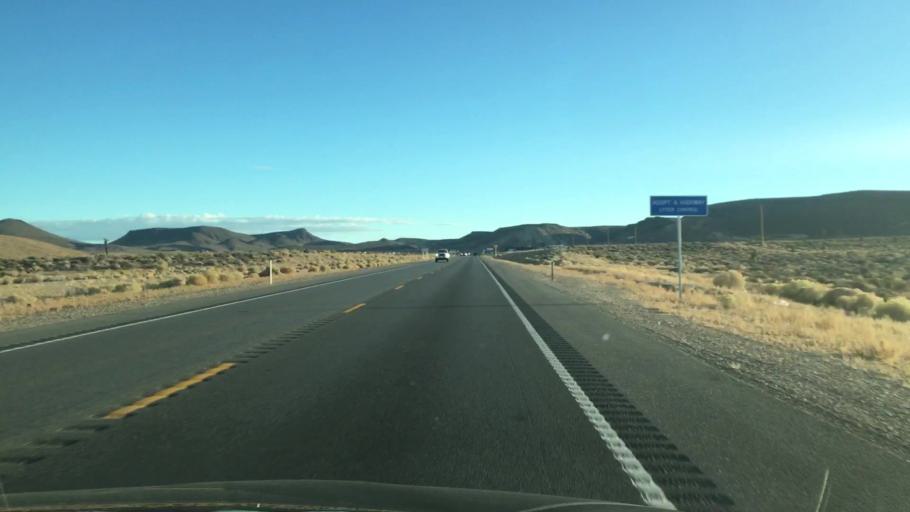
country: US
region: Nevada
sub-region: Esmeralda County
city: Goldfield
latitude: 37.7262
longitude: -117.2439
